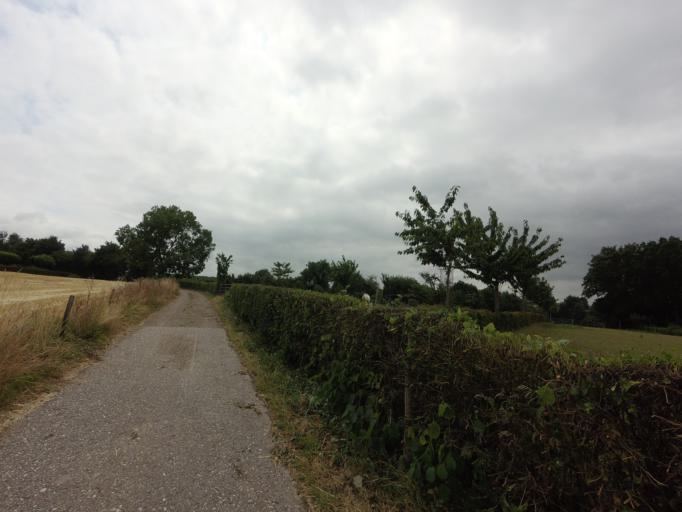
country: NL
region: Limburg
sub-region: Eijsden-Margraten
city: Margraten
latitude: 50.8159
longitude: 5.8007
